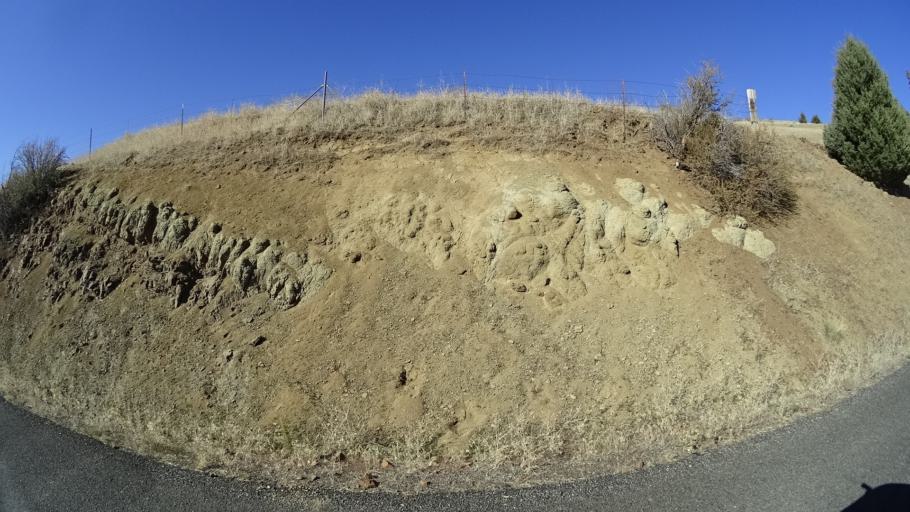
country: US
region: California
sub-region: Siskiyou County
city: Montague
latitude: 41.8239
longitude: -122.3409
